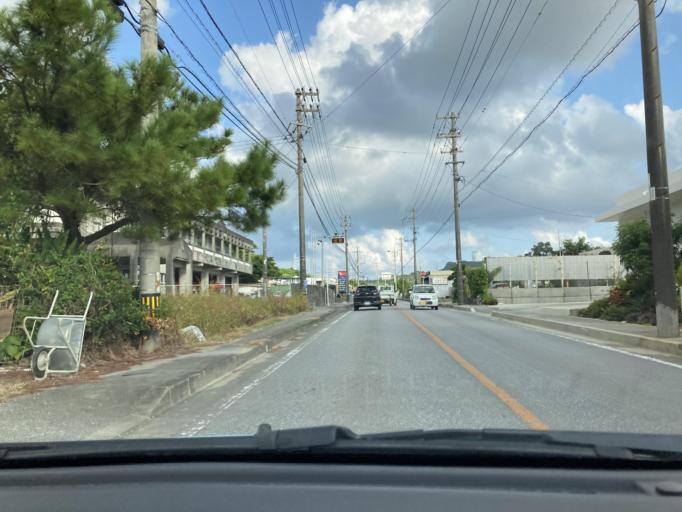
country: JP
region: Okinawa
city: Itoman
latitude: 26.1342
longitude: 127.6883
